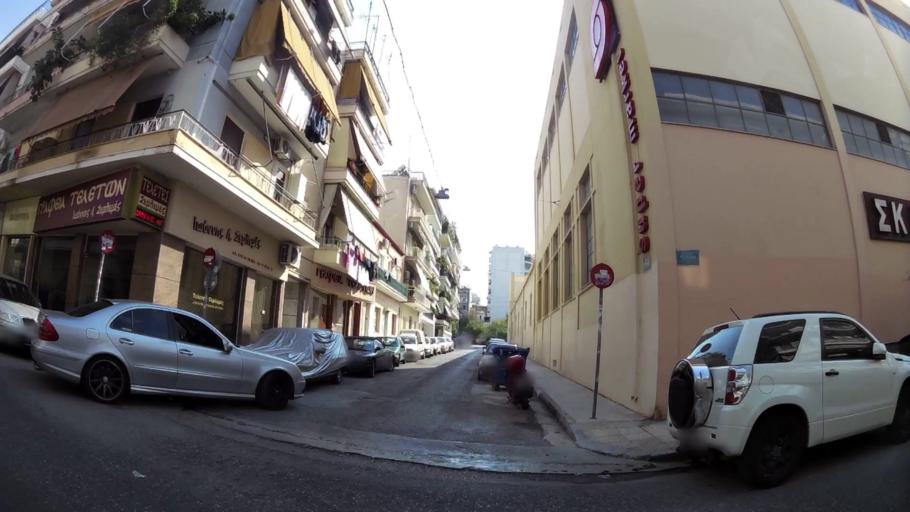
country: GR
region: Attica
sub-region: Nomarchia Athinas
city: Athens
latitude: 37.9675
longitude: 23.7073
